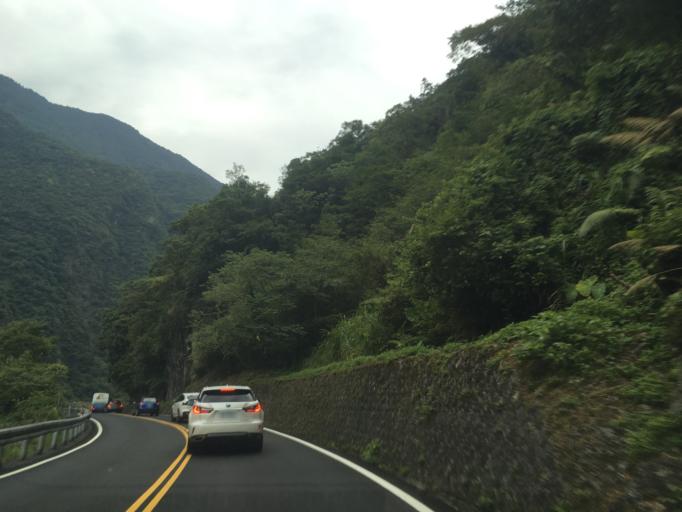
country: TW
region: Taiwan
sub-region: Hualien
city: Hualian
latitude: 24.1750
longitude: 121.5804
